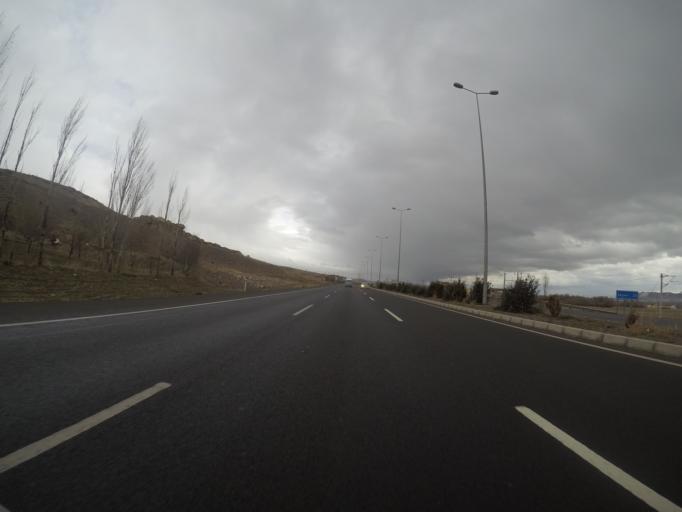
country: TR
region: Kayseri
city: Incesu
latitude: 38.7309
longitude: 35.2835
